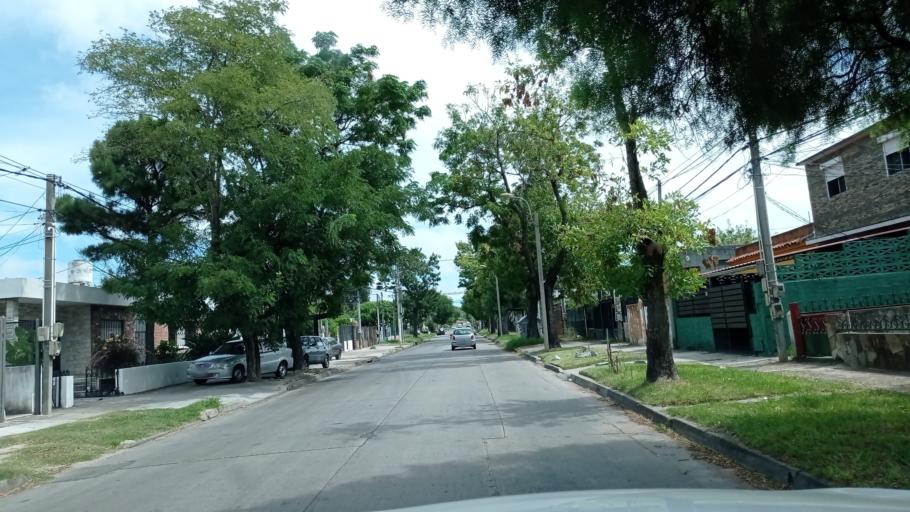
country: UY
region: Canelones
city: Paso de Carrasco
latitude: -34.8655
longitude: -56.1231
